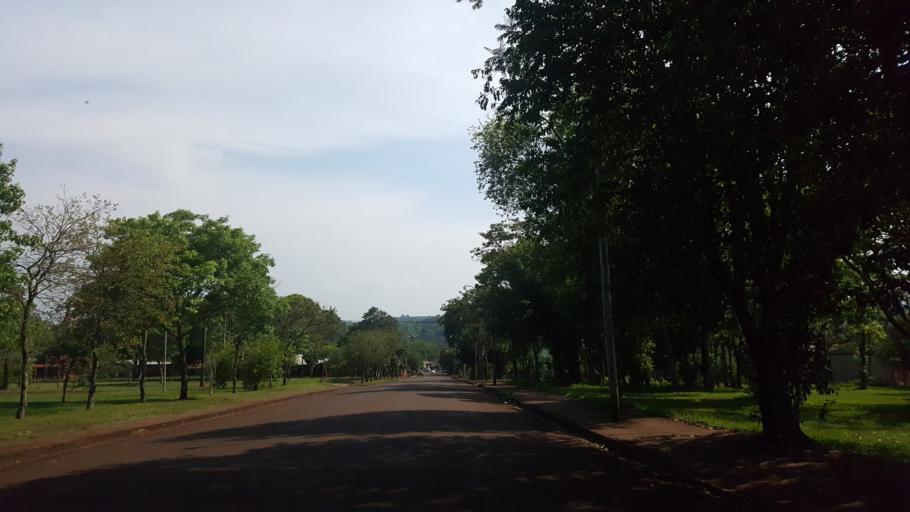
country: AR
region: Misiones
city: Capiovi
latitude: -26.9307
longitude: -55.0554
